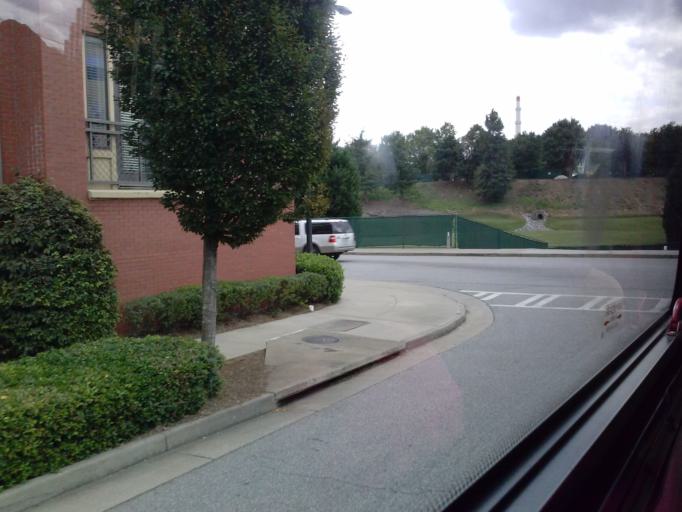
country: US
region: Georgia
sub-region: Fulton County
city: Atlanta
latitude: 33.7889
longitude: -84.4028
